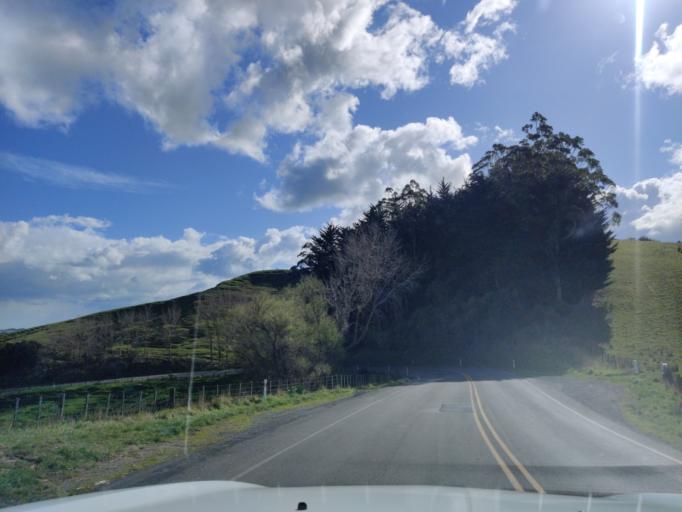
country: NZ
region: Manawatu-Wanganui
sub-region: Palmerston North City
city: Palmerston North
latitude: -40.2860
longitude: 175.7813
